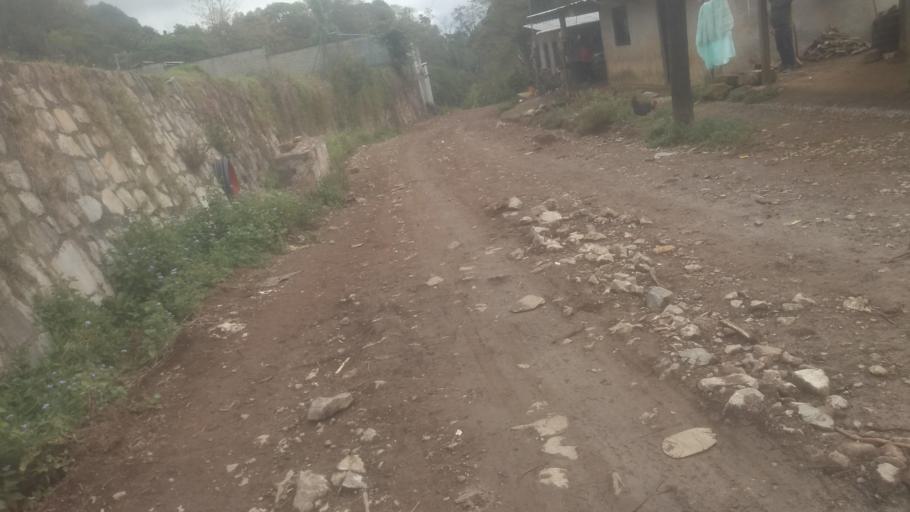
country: MX
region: Veracruz
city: Chocaman
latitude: 18.9881
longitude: -97.0576
